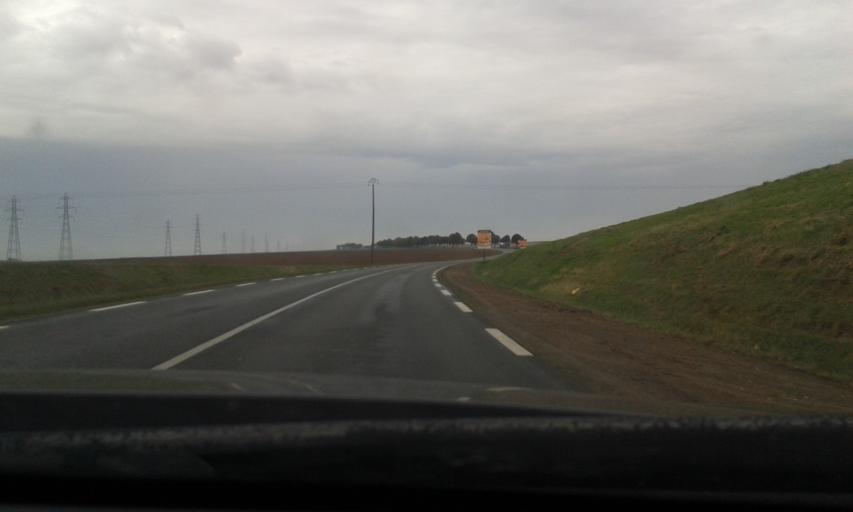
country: FR
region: Centre
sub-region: Departement d'Eure-et-Loir
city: Baigneaux
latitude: 48.1321
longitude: 1.8513
